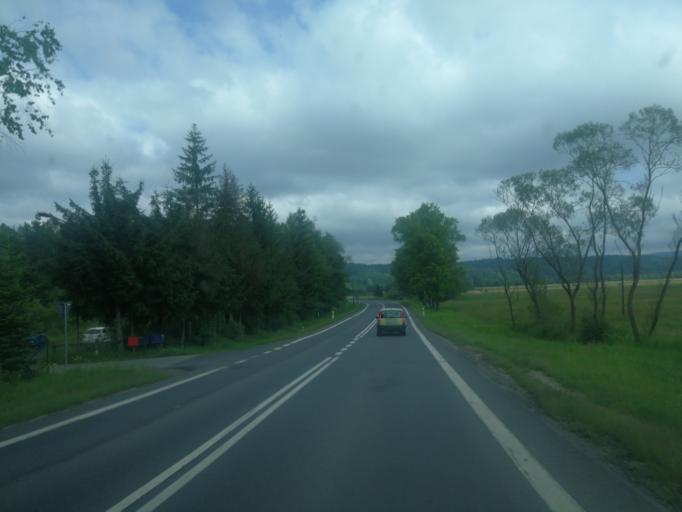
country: PL
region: Subcarpathian Voivodeship
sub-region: Powiat leski
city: Lesko
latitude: 49.4896
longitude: 22.3214
